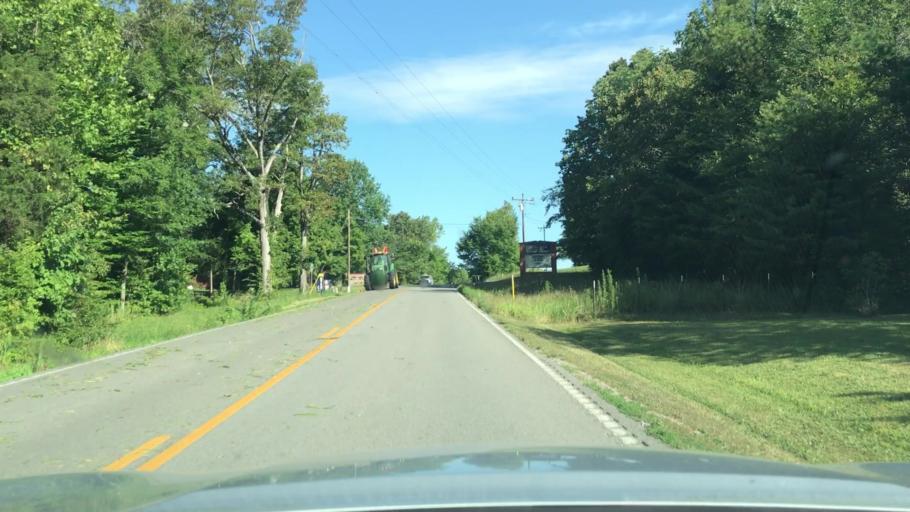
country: US
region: Kentucky
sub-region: Muhlenberg County
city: Greenville
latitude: 37.1312
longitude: -87.1402
